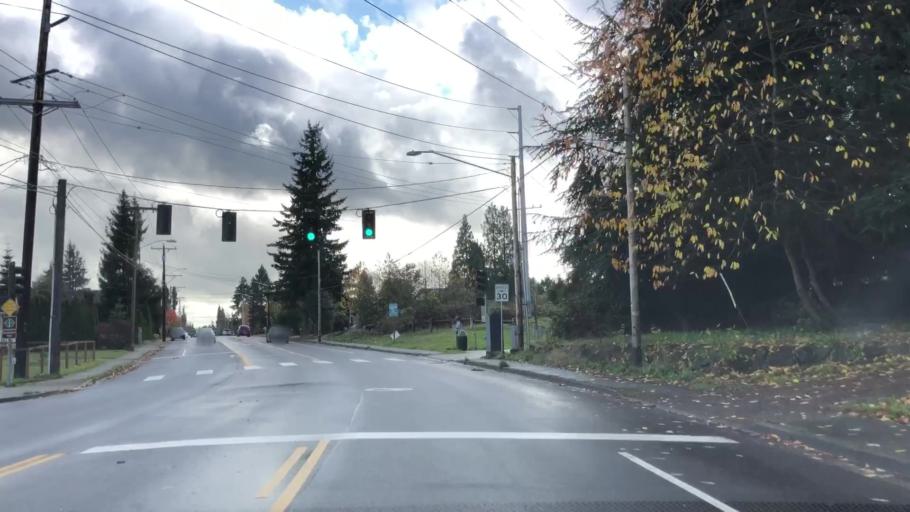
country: US
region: Washington
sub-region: Snohomish County
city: Everett
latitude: 47.9285
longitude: -122.2116
